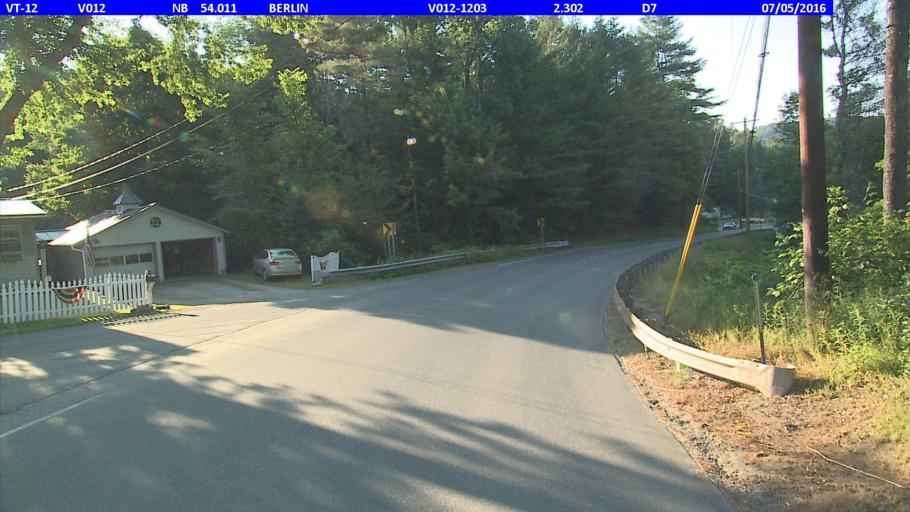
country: US
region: Vermont
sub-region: Washington County
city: Northfield
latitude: 44.2026
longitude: -72.6367
